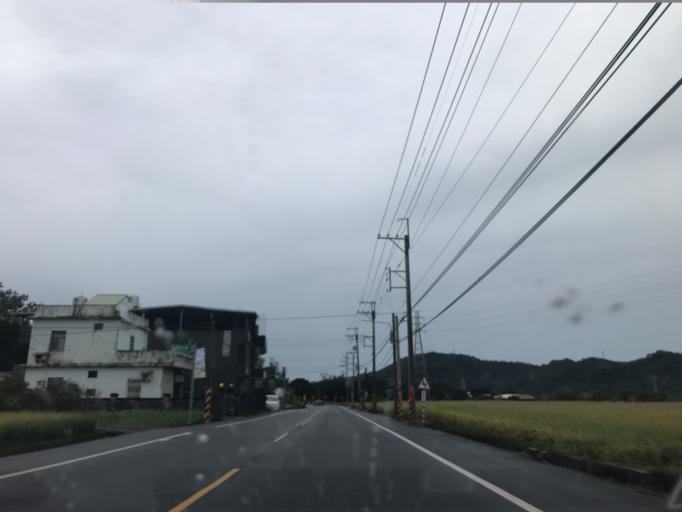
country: TW
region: Taiwan
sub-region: Hsinchu
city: Zhubei
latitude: 24.8398
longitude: 121.1111
